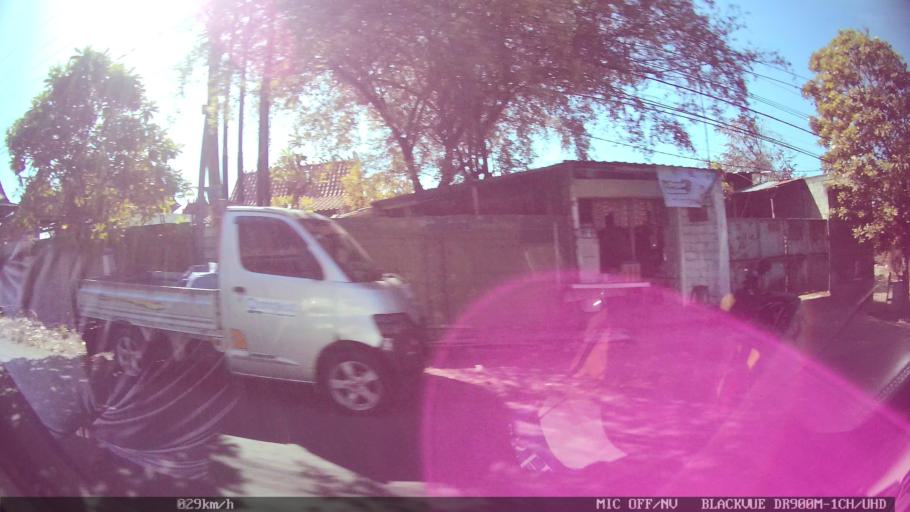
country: ID
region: Bali
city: Banjar Kertasari
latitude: -8.6328
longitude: 115.1897
